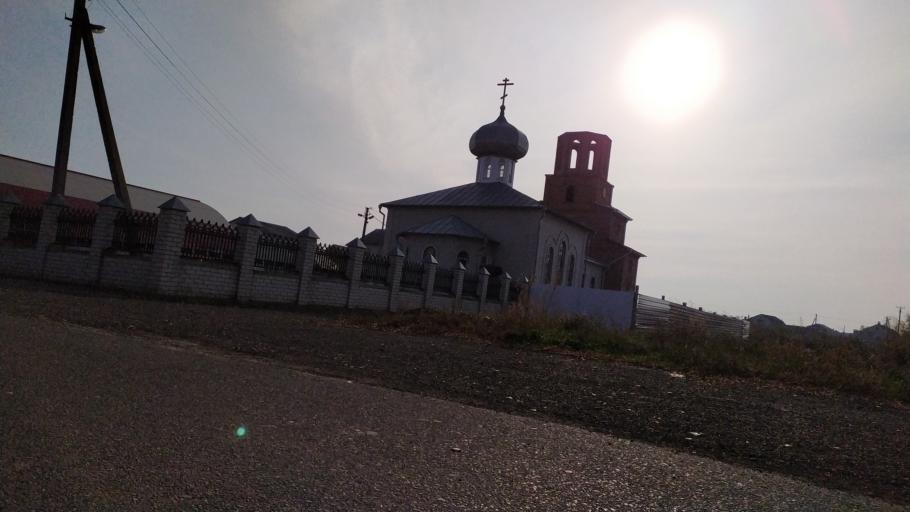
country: RU
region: Kursk
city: Kursk
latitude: 51.6420
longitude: 36.1507
